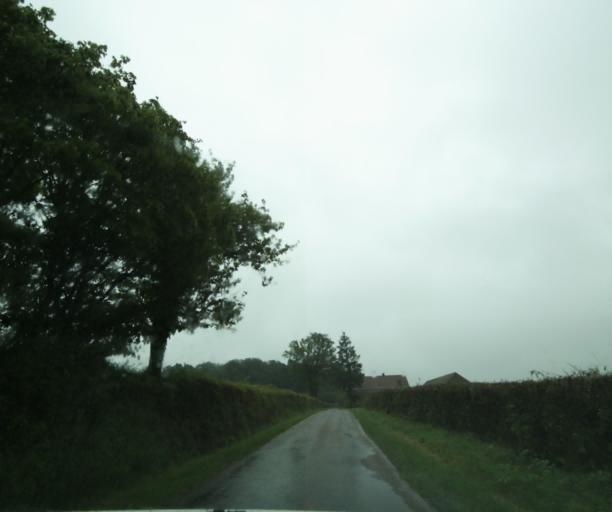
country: FR
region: Bourgogne
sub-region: Departement de Saone-et-Loire
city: Charolles
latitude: 46.4063
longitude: 4.2462
